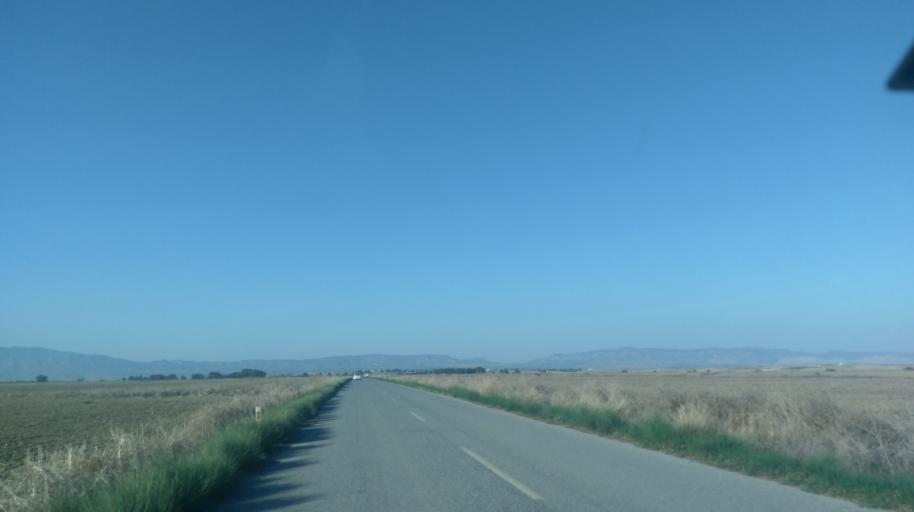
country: CY
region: Ammochostos
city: Lefkonoiko
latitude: 35.1863
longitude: 33.6998
